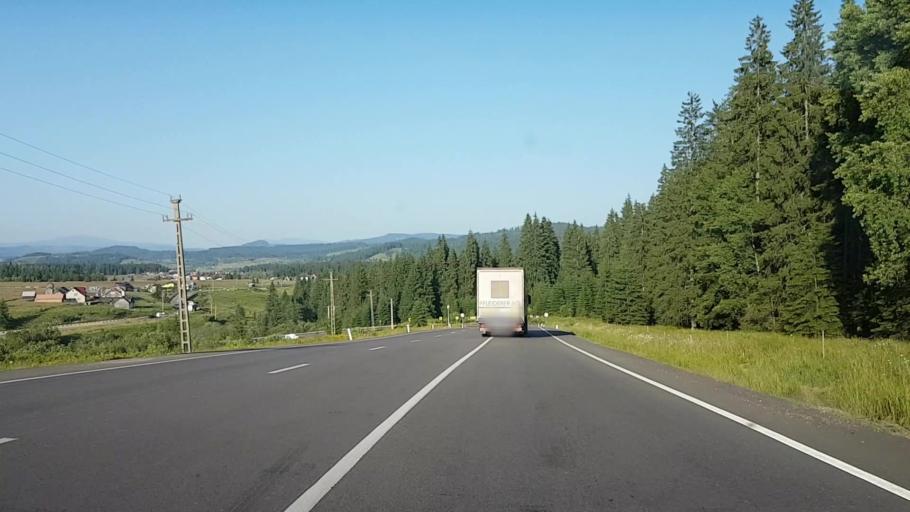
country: RO
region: Suceava
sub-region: Comuna Poiana Stampei
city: Poiana Stampei
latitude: 47.2982
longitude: 25.0920
